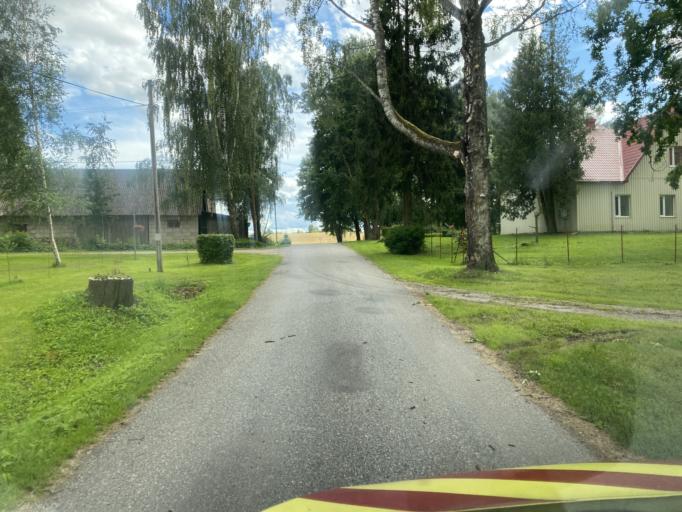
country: EE
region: Viljandimaa
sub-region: Viiratsi vald
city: Viiratsi
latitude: 58.3935
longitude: 25.8213
